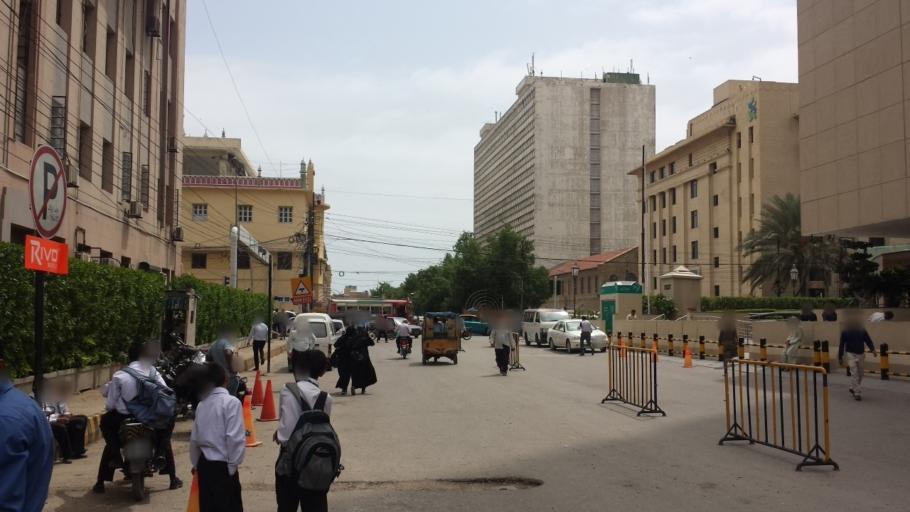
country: PK
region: Sindh
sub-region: Karachi District
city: Karachi
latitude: 24.8502
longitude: 67.0058
